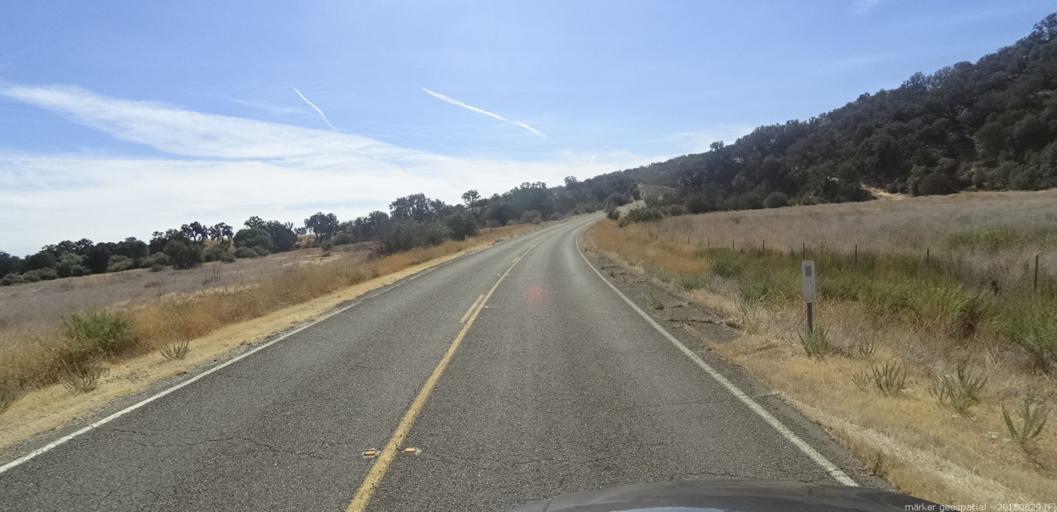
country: US
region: California
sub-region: San Luis Obispo County
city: Lake Nacimiento
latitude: 35.8868
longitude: -121.0695
